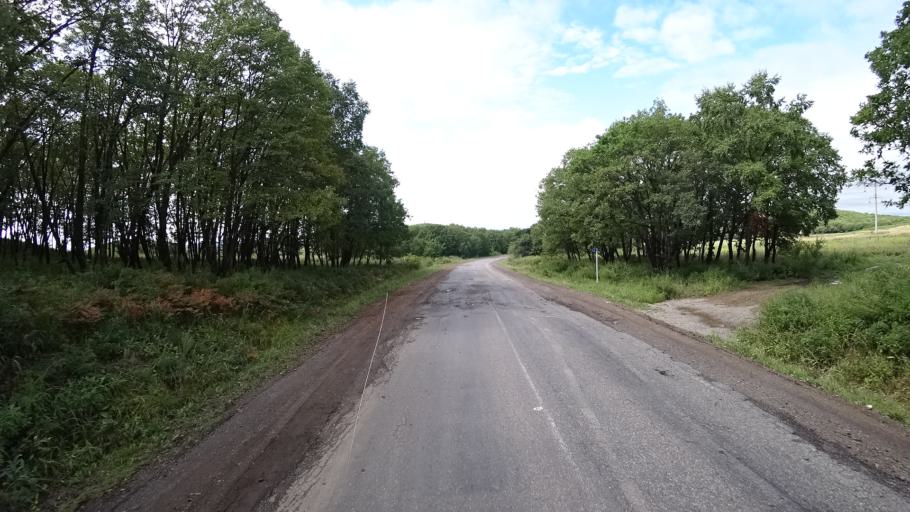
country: RU
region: Primorskiy
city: Lyalichi
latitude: 44.1423
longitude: 132.4051
